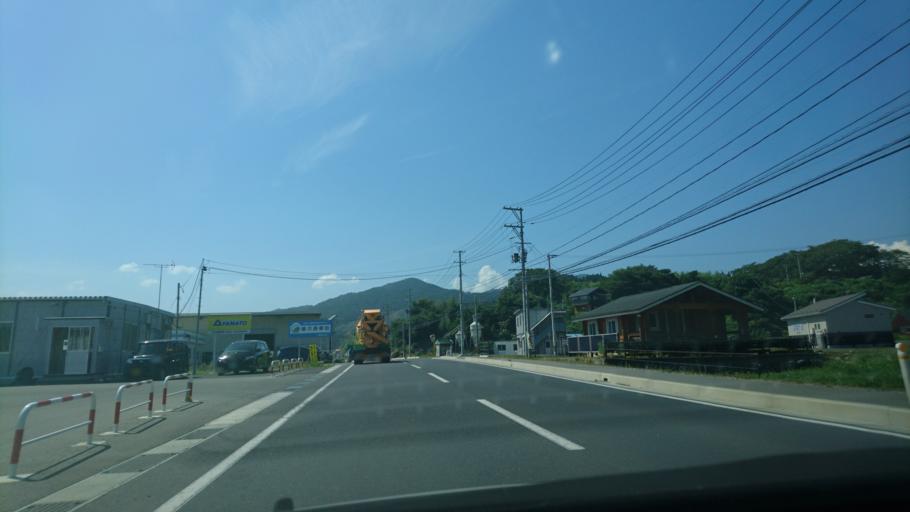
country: JP
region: Iwate
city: Ofunato
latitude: 39.0336
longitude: 141.6121
